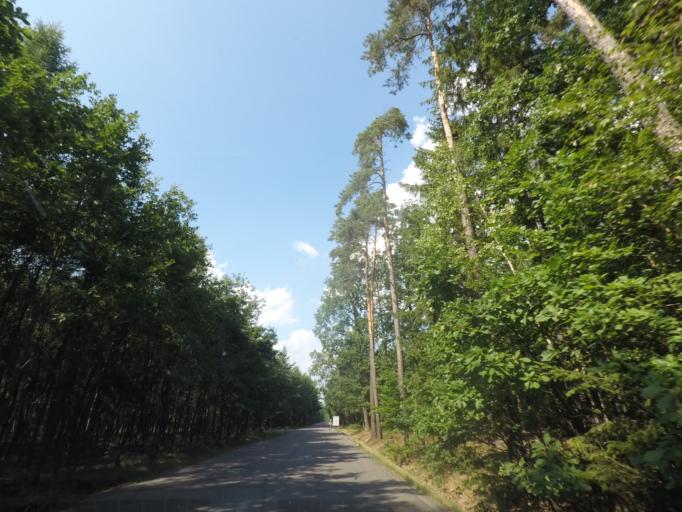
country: CZ
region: Pardubicky
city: Horni Jeleni
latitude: 50.0630
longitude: 16.0826
